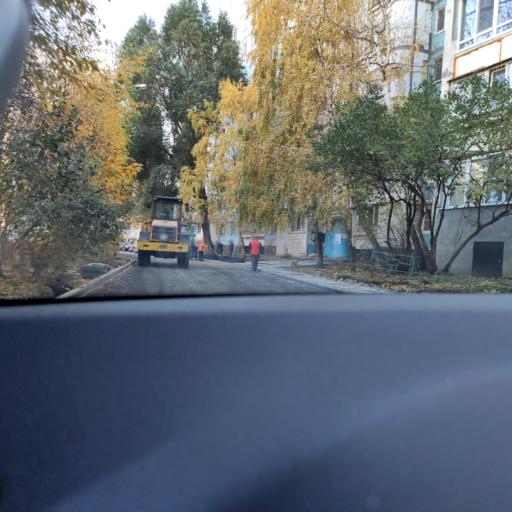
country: RU
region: Samara
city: Samara
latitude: 53.2486
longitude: 50.2109
